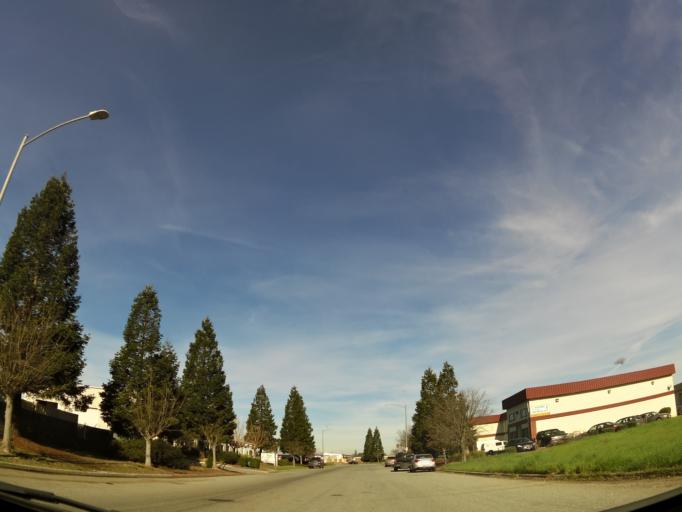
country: US
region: California
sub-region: Santa Clara County
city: Gilroy
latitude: 37.0255
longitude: -121.5745
